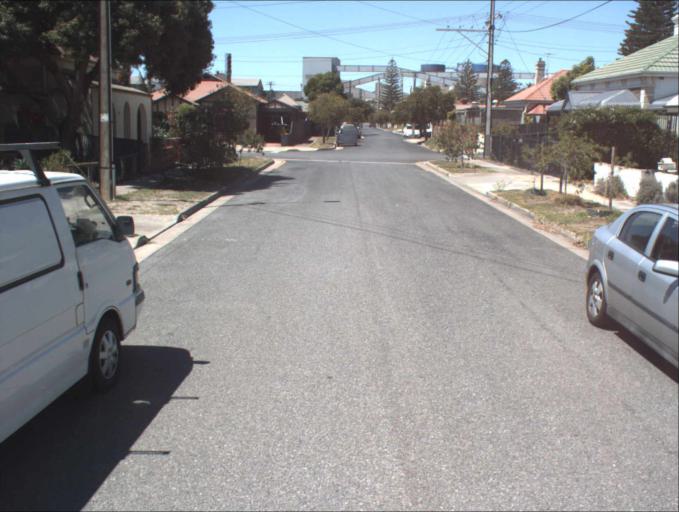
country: AU
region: South Australia
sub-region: Port Adelaide Enfield
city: Birkenhead
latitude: -34.8340
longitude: 138.4983
